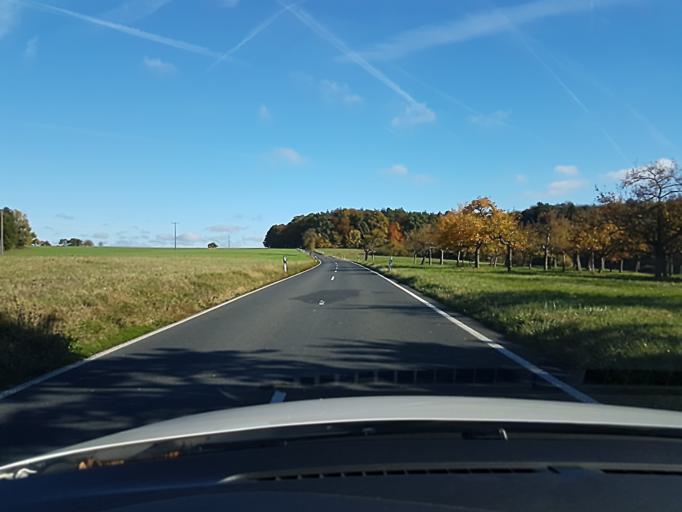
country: DE
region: Bavaria
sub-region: Regierungsbezirk Unterfranken
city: Hausen
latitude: 49.8771
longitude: 9.2312
